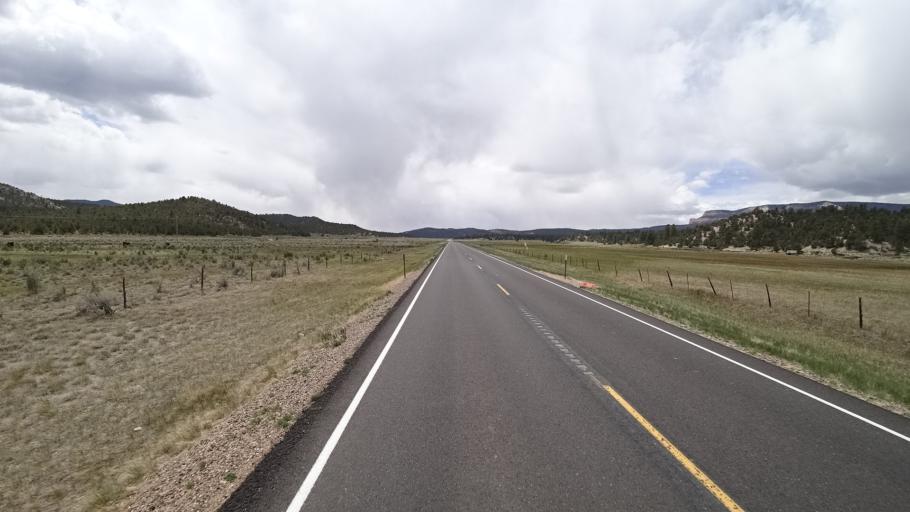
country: US
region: Utah
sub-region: Garfield County
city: Panguitch
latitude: 37.6902
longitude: -111.8024
